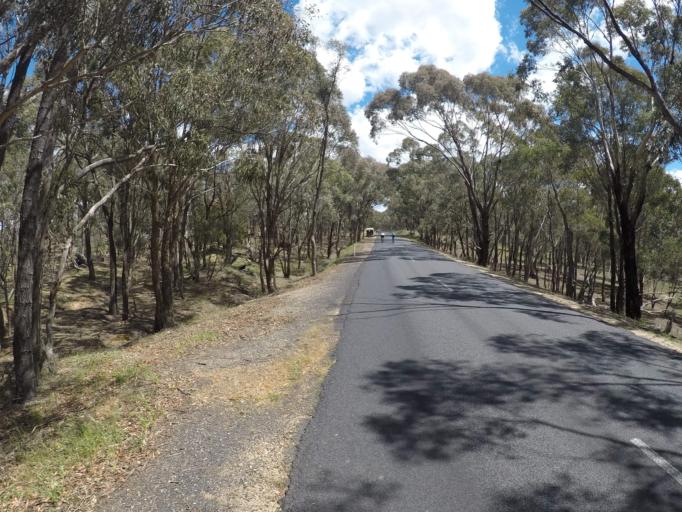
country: AU
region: New South Wales
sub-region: Blayney
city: Blayney
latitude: -33.5805
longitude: 149.3957
